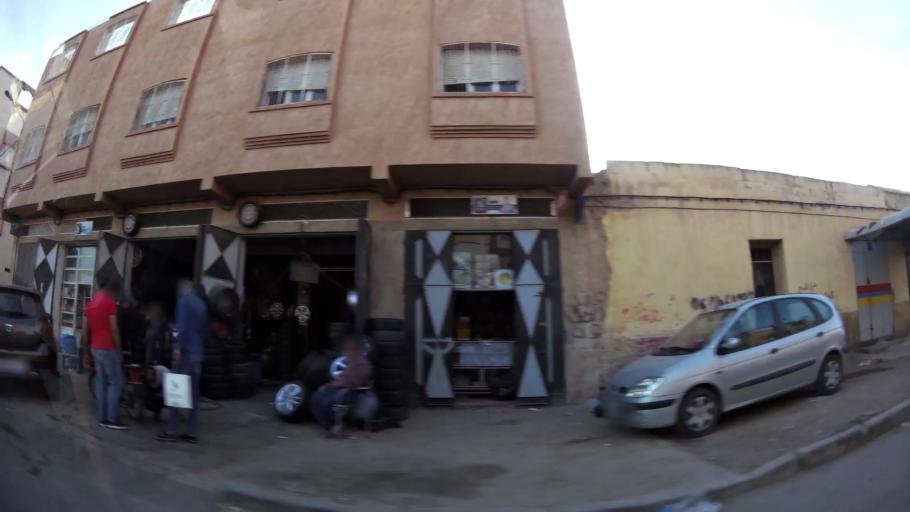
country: MA
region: Oriental
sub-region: Oujda-Angad
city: Oujda
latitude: 34.6768
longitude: -1.8825
